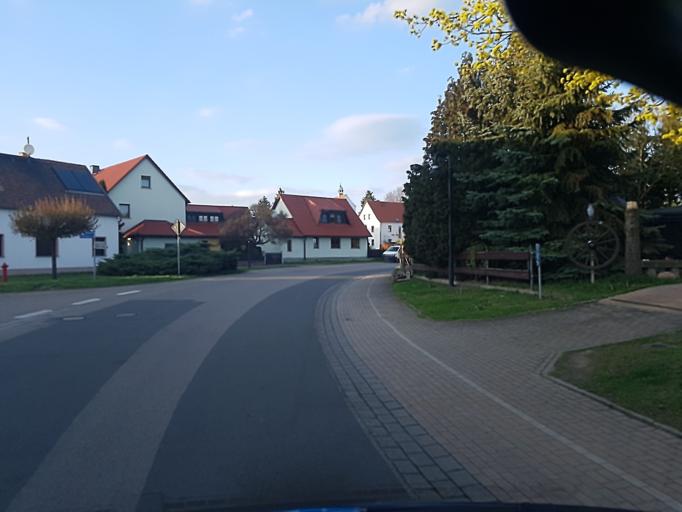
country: DE
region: Saxony
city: Trossin
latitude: 51.5680
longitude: 12.8463
